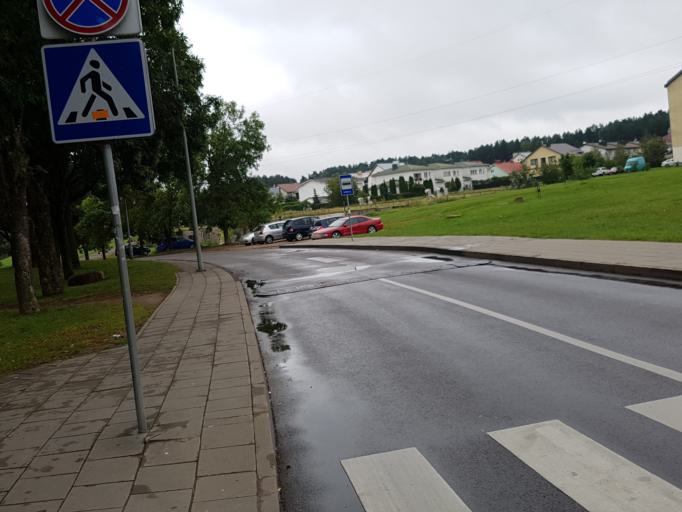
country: LT
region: Vilnius County
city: Lazdynai
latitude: 54.6678
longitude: 25.2164
